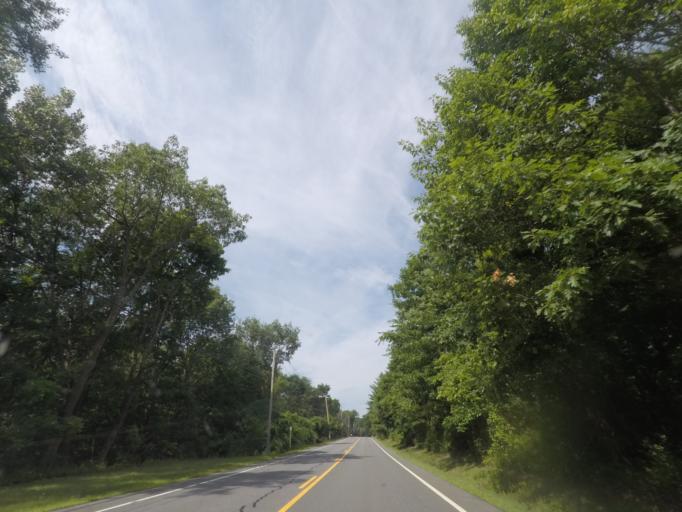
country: US
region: New York
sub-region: Rensselaer County
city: Wynantskill
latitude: 42.7324
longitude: -73.6366
